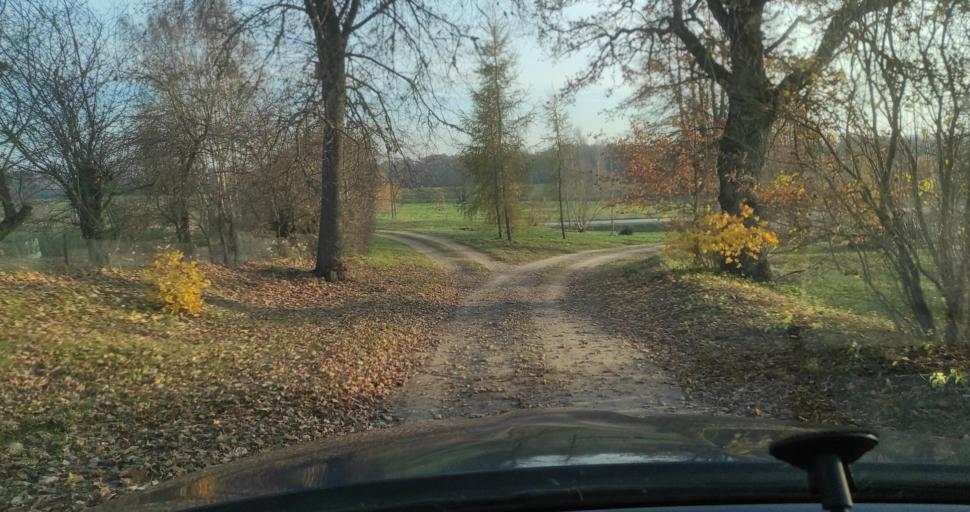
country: LV
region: Aizpute
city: Aizpute
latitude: 56.7502
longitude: 21.7975
